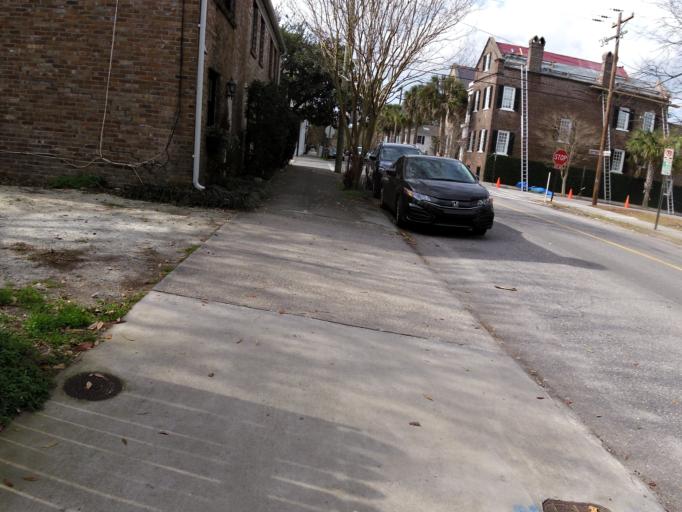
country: US
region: South Carolina
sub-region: Charleston County
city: Charleston
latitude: 32.7773
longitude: -79.9371
